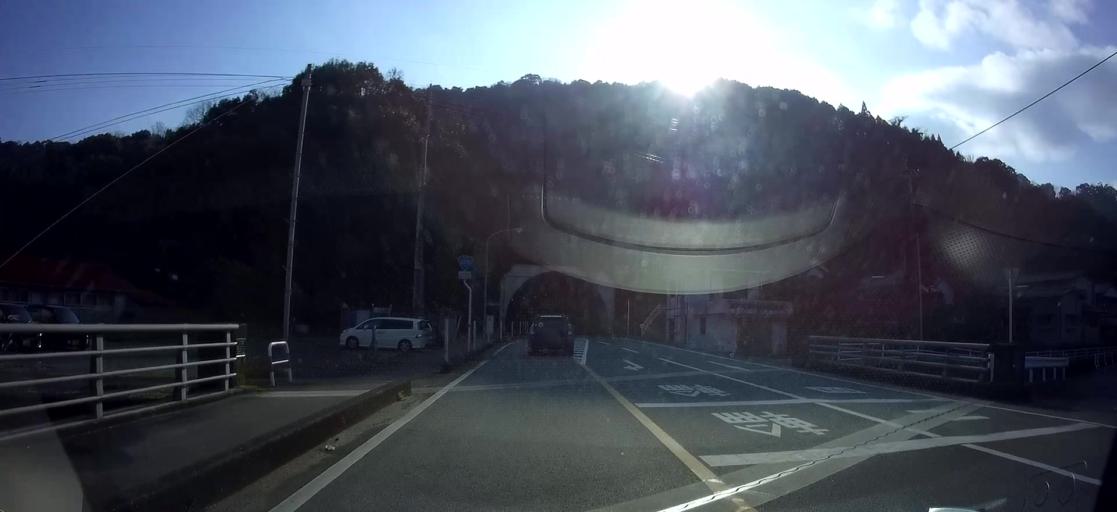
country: JP
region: Kumamoto
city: Yatsushiro
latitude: 32.4411
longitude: 130.4058
